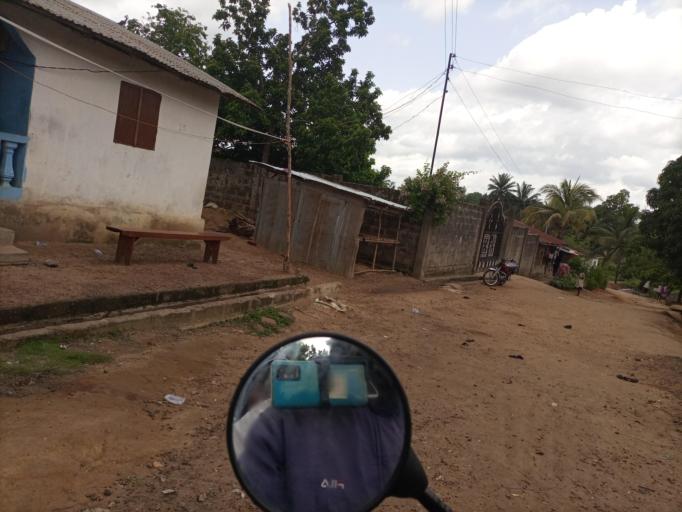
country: SL
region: Southern Province
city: Bo
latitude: 7.9477
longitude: -11.7331
